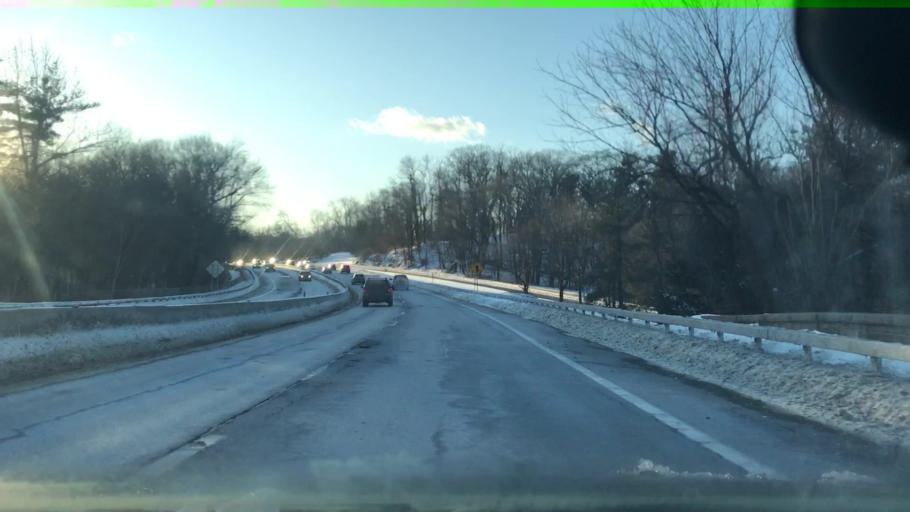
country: US
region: New York
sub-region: Westchester County
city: Scarsdale
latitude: 40.9690
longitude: -73.7764
